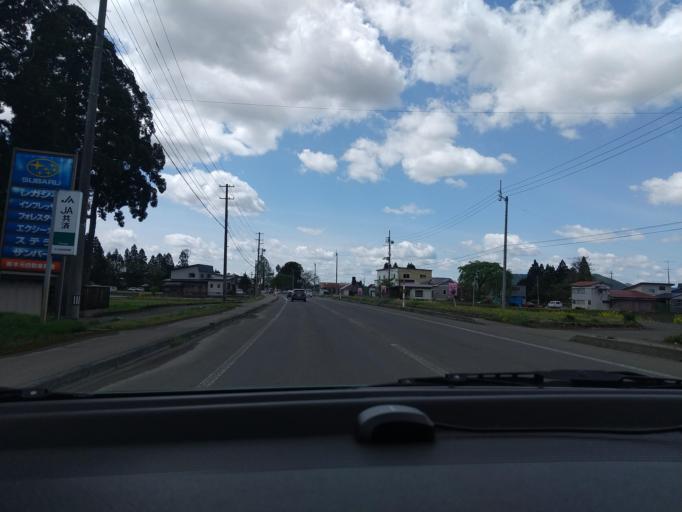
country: JP
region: Akita
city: Kakunodatemachi
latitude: 39.5734
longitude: 140.5631
